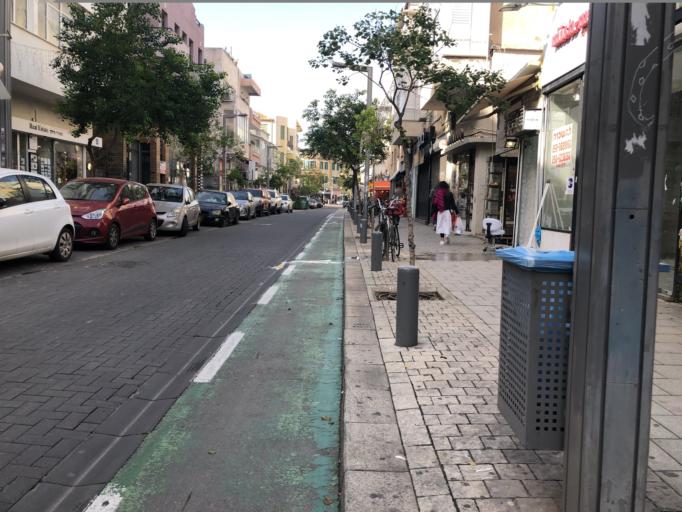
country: IL
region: Tel Aviv
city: Tel Aviv
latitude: 32.0695
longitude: 34.7720
